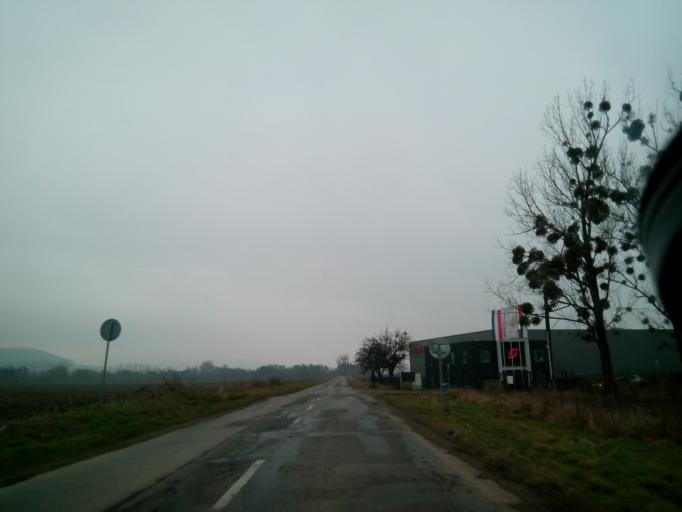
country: SK
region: Kosicky
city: Kosice
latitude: 48.7276
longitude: 21.4386
